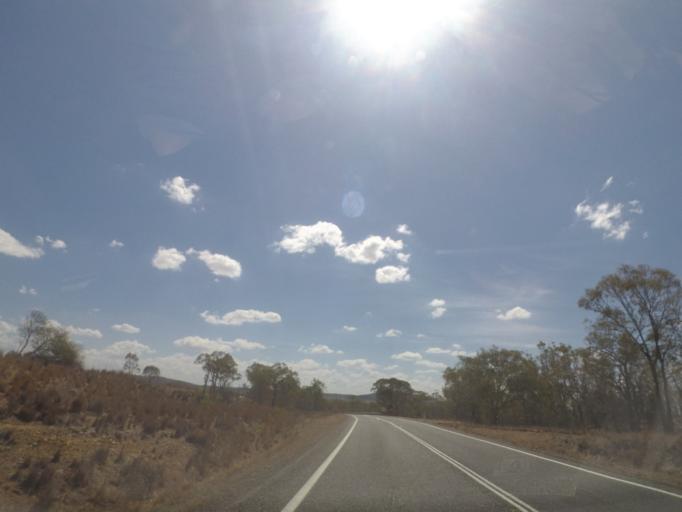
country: AU
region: Queensland
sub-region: Southern Downs
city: Warwick
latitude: -28.2053
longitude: 151.5742
